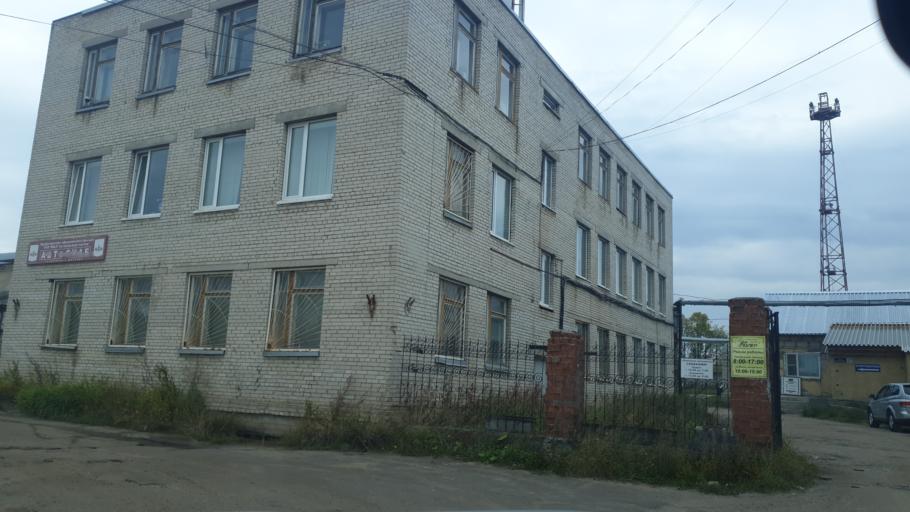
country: RU
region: Komi Republic
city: Ezhva
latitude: 61.8121
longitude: 50.7459
